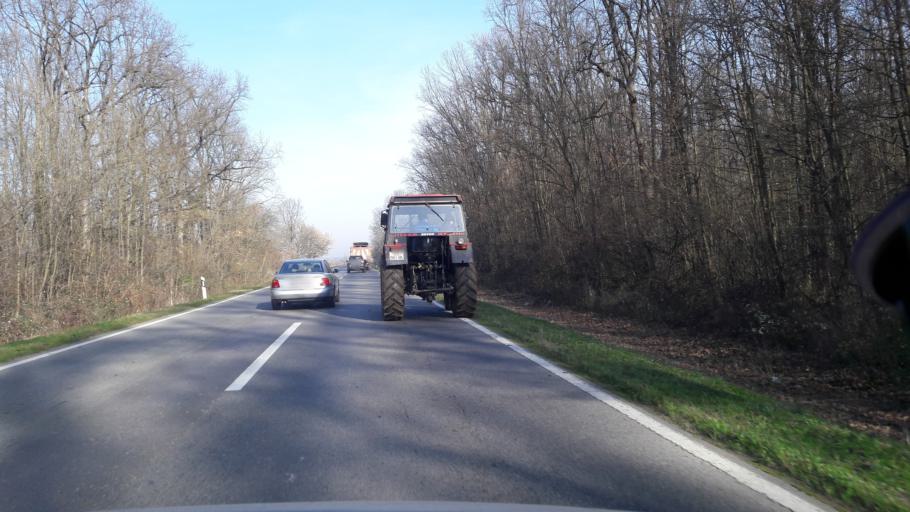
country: HR
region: Vukovarsko-Srijemska
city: Gradiste
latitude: 45.1305
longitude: 18.7174
